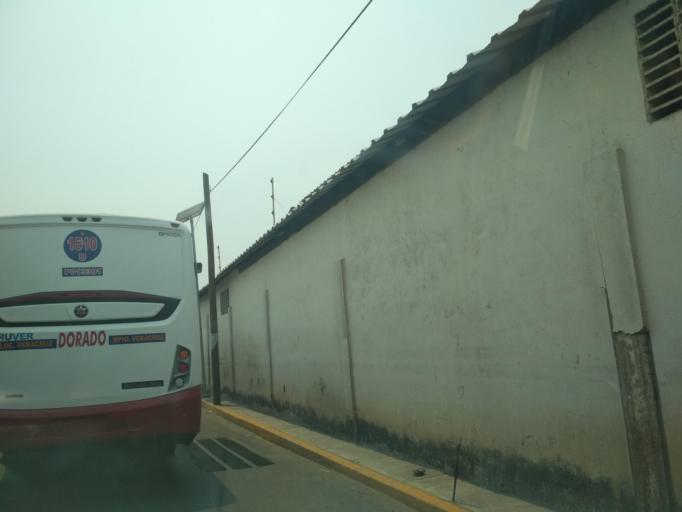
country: MX
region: Veracruz
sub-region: Veracruz
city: Las Amapolas
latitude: 19.1601
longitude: -96.2008
